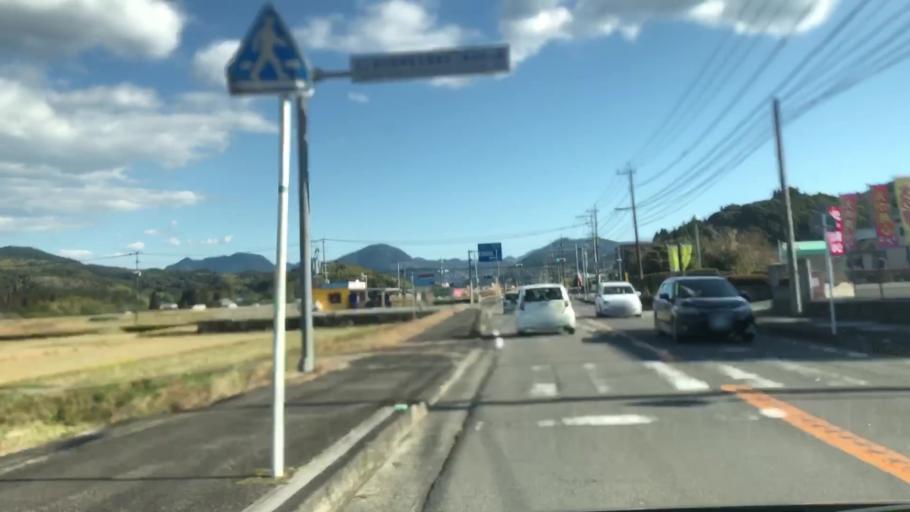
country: JP
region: Kagoshima
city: Satsumasendai
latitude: 31.7988
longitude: 130.4311
